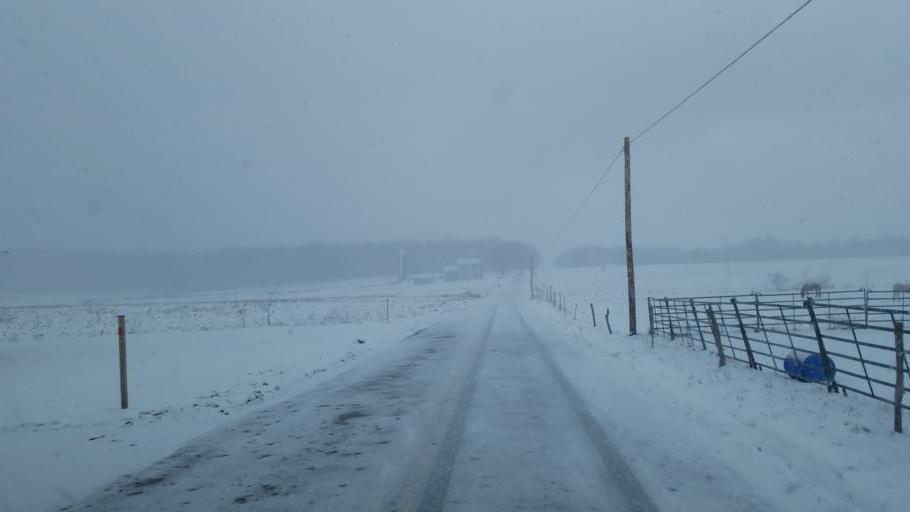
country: US
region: Pennsylvania
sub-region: Crawford County
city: Cochranton
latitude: 41.4399
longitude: -80.0124
